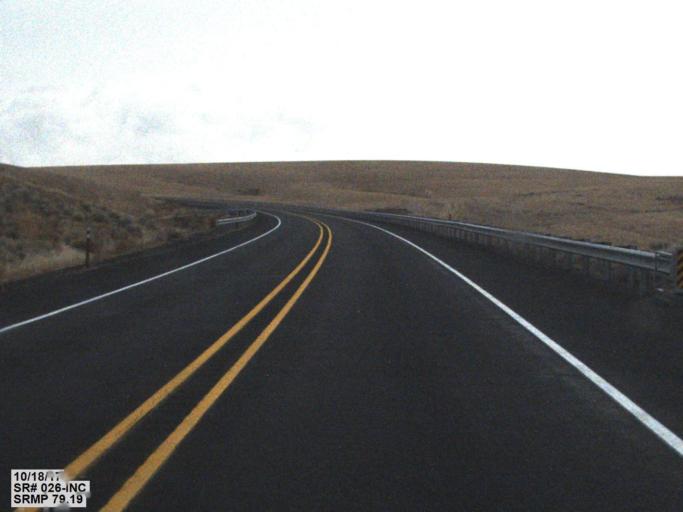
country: US
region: Washington
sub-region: Adams County
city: Ritzville
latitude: 46.7791
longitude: -118.3795
